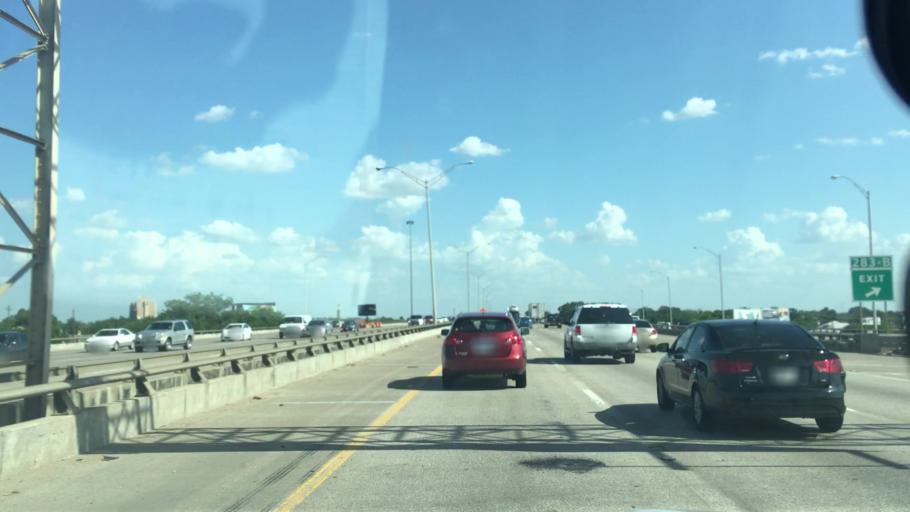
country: US
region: Texas
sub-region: Dallas County
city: Dallas
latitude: 32.7697
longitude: -96.7777
